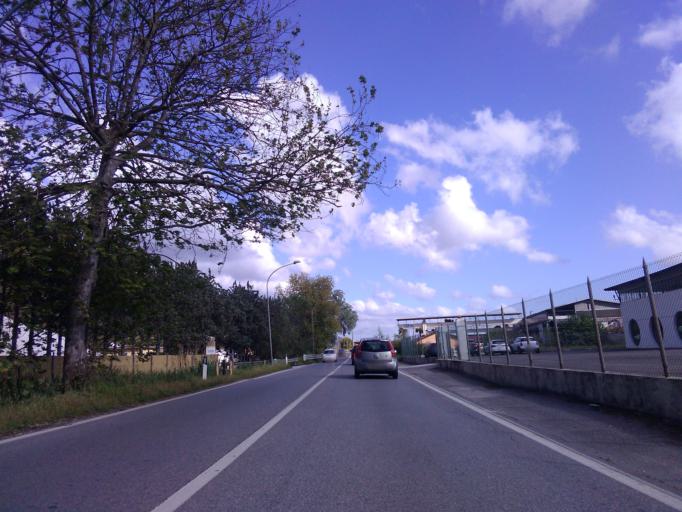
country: IT
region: Tuscany
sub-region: Provincia di Lucca
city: Strettoia
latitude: 43.9946
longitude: 10.1773
